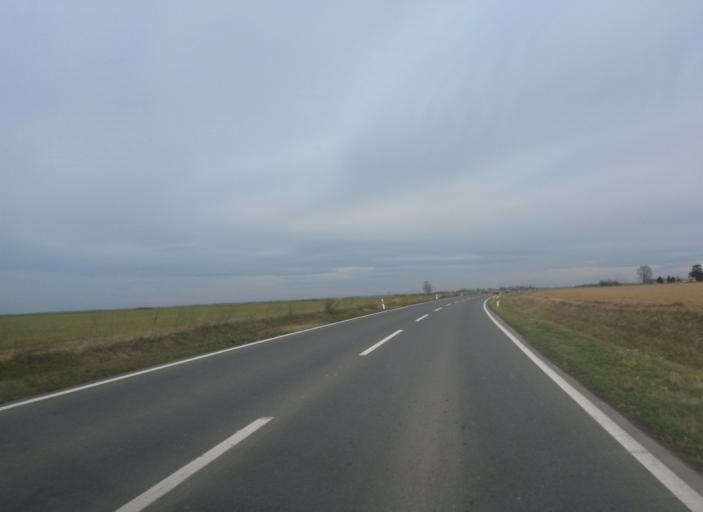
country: HR
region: Osjecko-Baranjska
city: Cepin
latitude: 45.5227
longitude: 18.5385
